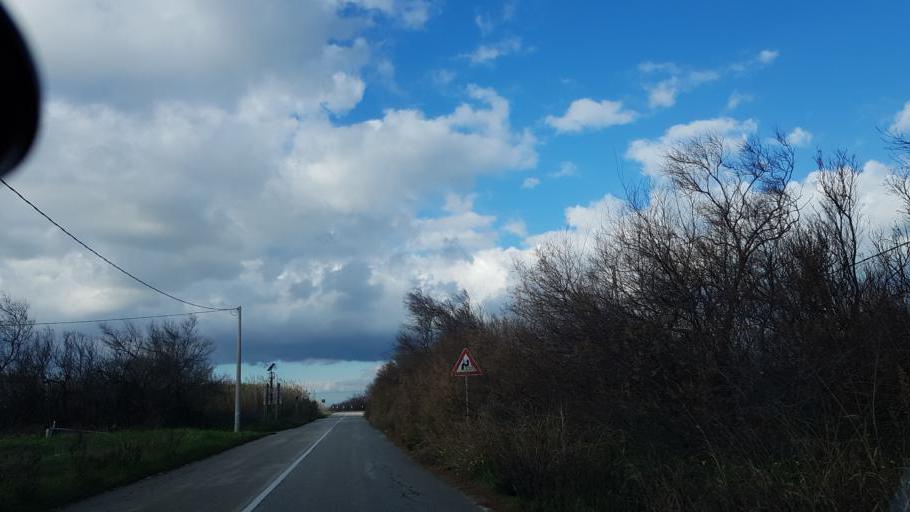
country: IT
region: Apulia
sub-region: Provincia di Brindisi
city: Materdomini
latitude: 40.6790
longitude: 17.9275
